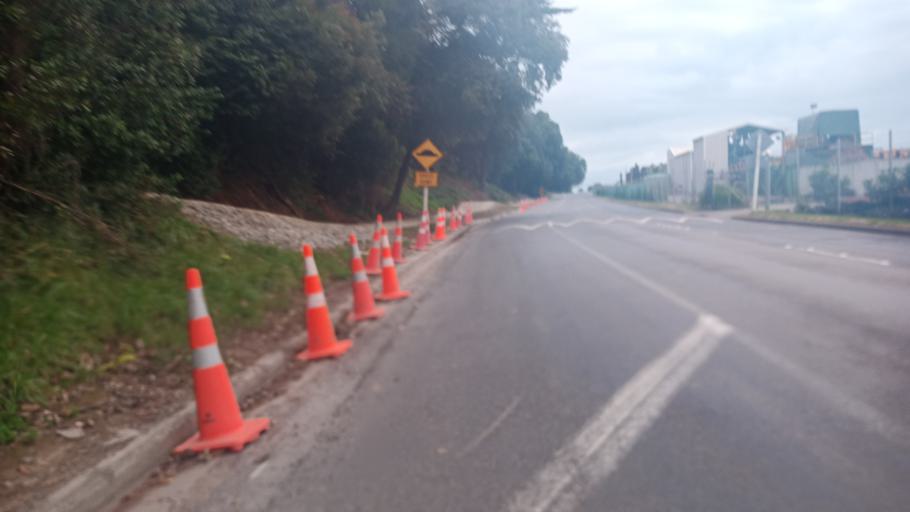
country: NZ
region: Gisborne
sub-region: Gisborne District
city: Gisborne
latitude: -38.6763
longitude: 178.0262
